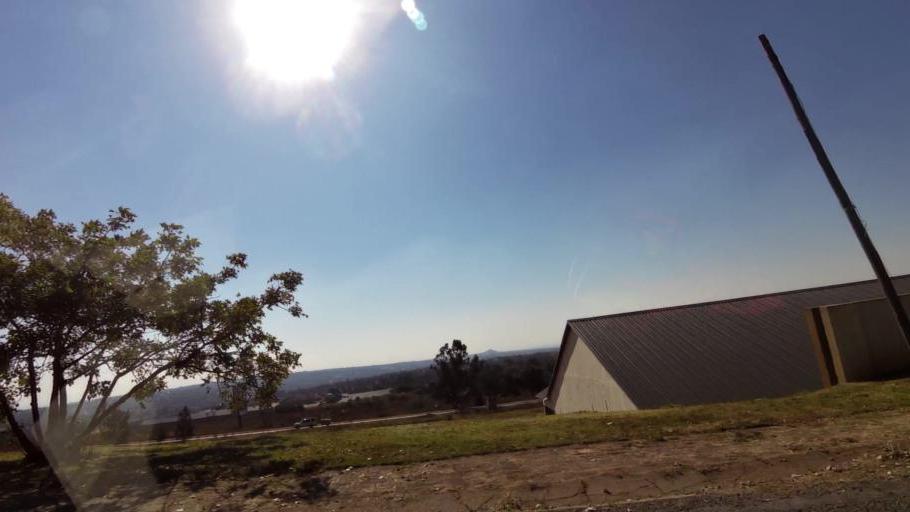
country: ZA
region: Gauteng
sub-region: City of Johannesburg Metropolitan Municipality
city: Roodepoort
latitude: -26.1531
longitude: 27.9367
